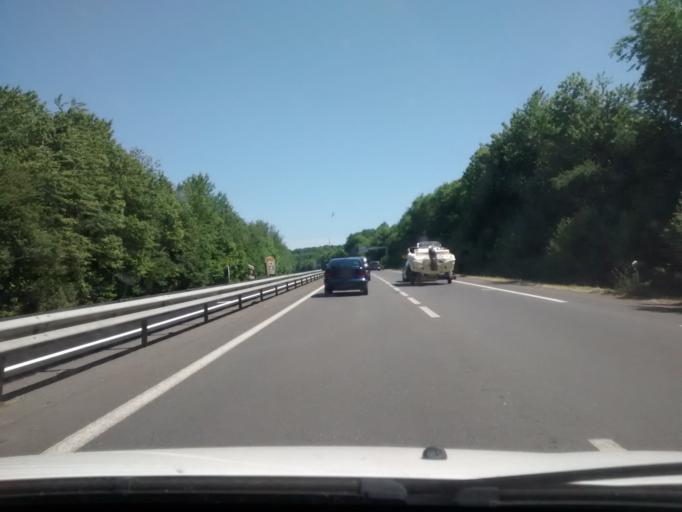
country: FR
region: Brittany
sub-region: Departement d'Ille-et-Vilaine
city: Hede-Bazouges
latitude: 48.3015
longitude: -1.8266
